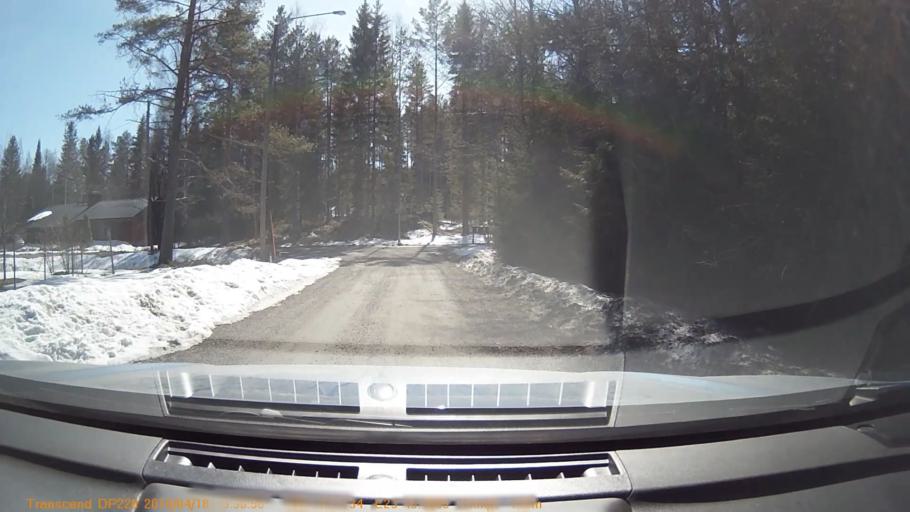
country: FI
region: Pirkanmaa
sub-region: Tampere
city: Kuru
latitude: 61.8685
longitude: 23.7235
